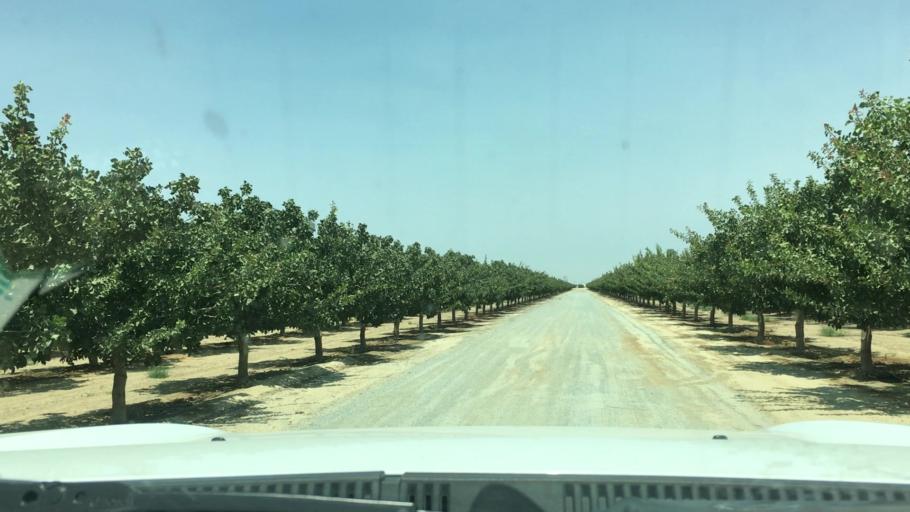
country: US
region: California
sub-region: Kern County
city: Wasco
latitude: 35.6750
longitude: -119.4286
